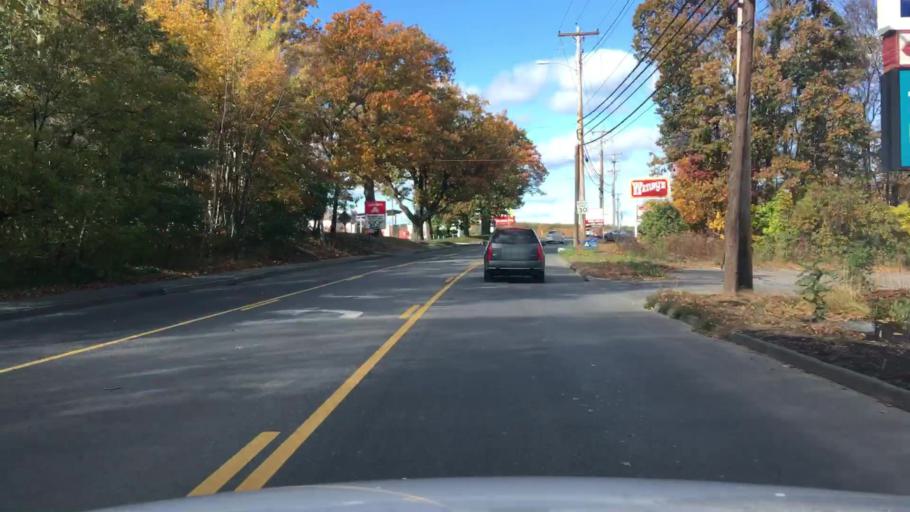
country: US
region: Maine
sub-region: Kennebec County
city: Waterville
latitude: 44.5644
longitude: -69.6366
